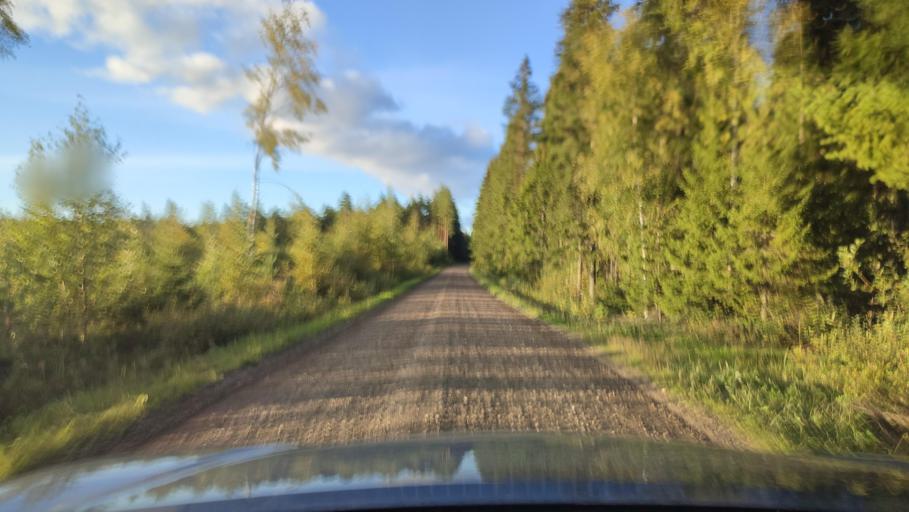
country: FI
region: Southern Ostrobothnia
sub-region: Suupohja
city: Karijoki
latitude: 62.2268
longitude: 21.5722
